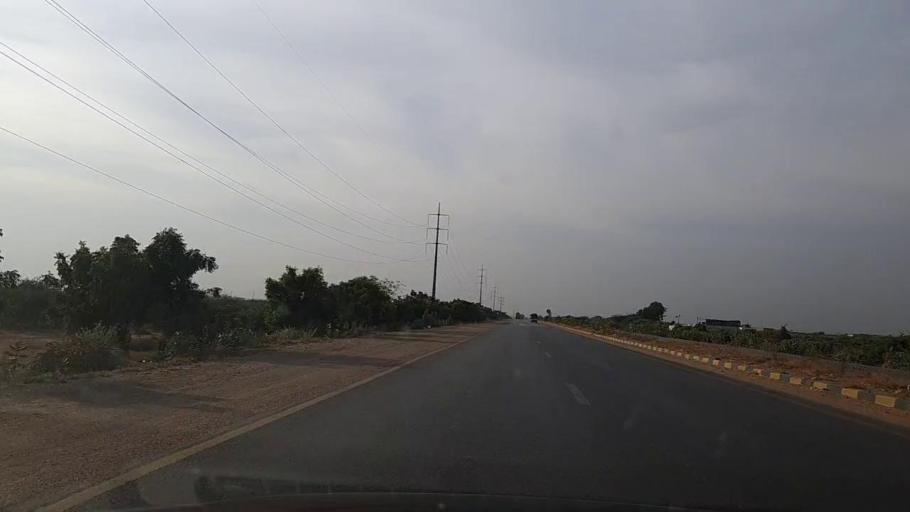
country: PK
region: Sindh
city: Gharo
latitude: 24.8323
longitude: 67.4613
